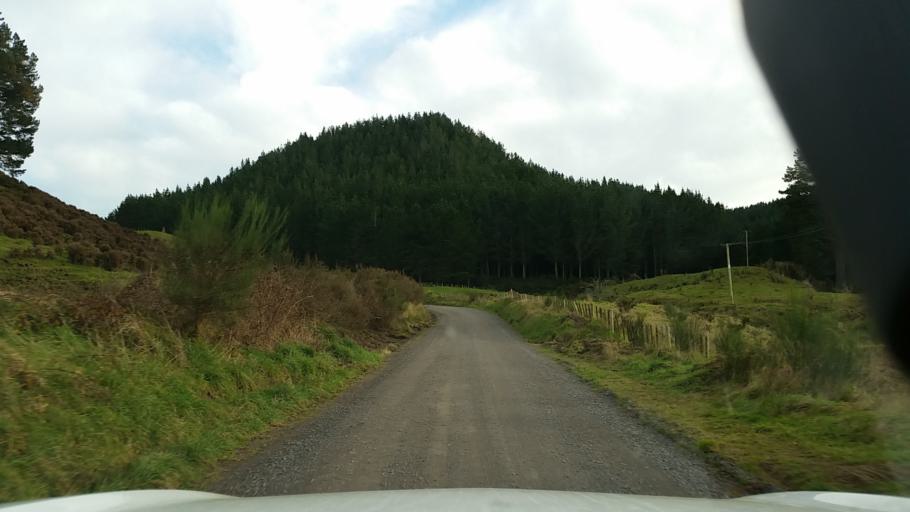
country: NZ
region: Bay of Plenty
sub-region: Rotorua District
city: Rotorua
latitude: -38.2257
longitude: 176.1618
